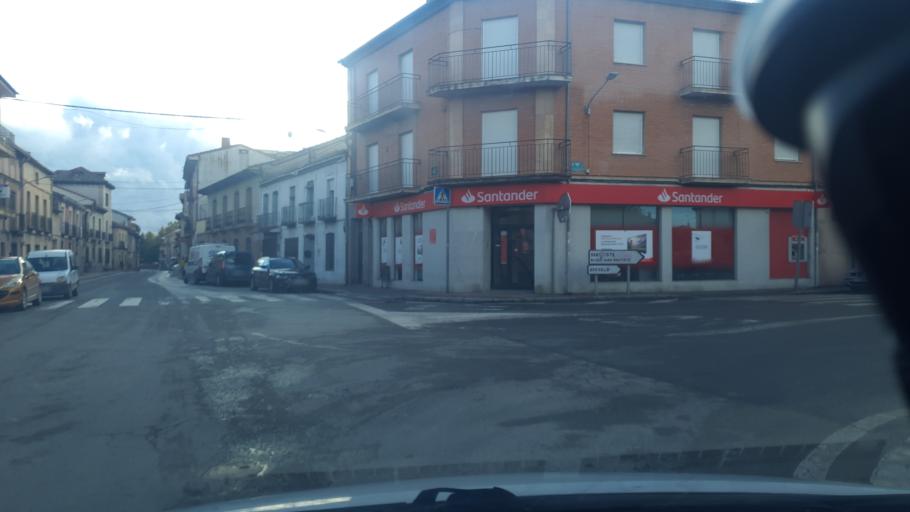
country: ES
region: Castille and Leon
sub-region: Provincia de Segovia
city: Nava de la Asuncion
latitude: 41.1569
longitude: -4.4872
